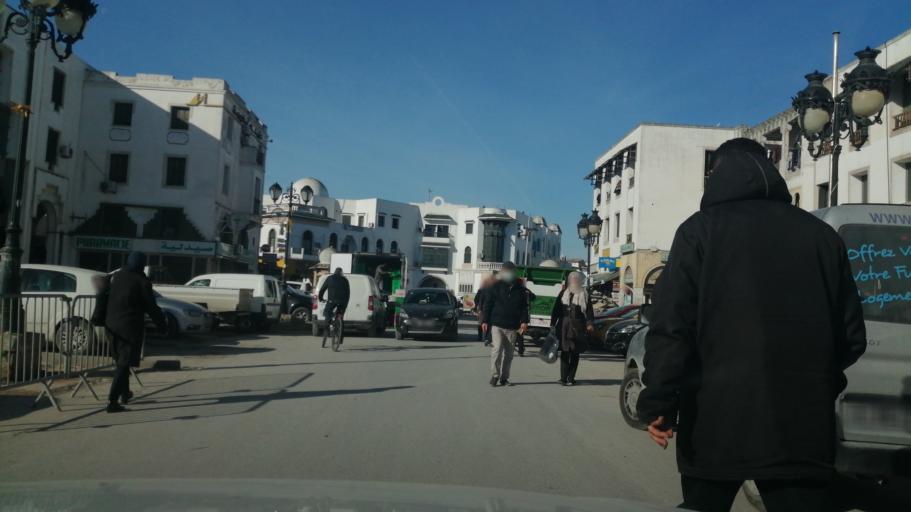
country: TN
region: Tunis
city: Tunis
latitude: 36.8053
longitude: 10.1689
